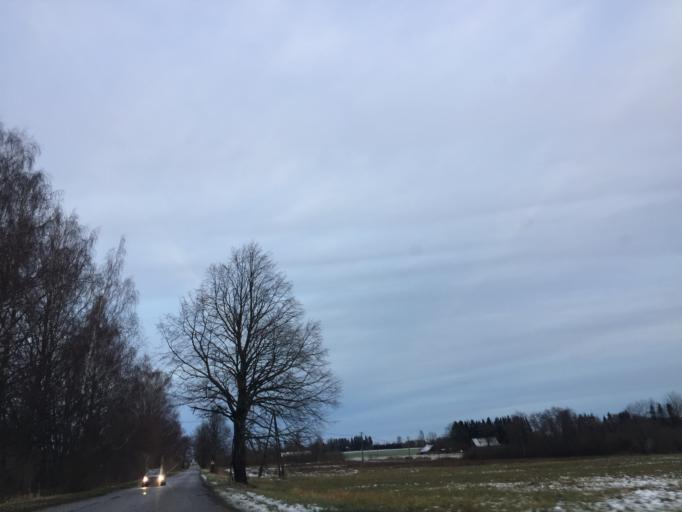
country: LV
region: Aloja
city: Aloja
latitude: 57.6019
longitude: 24.8604
